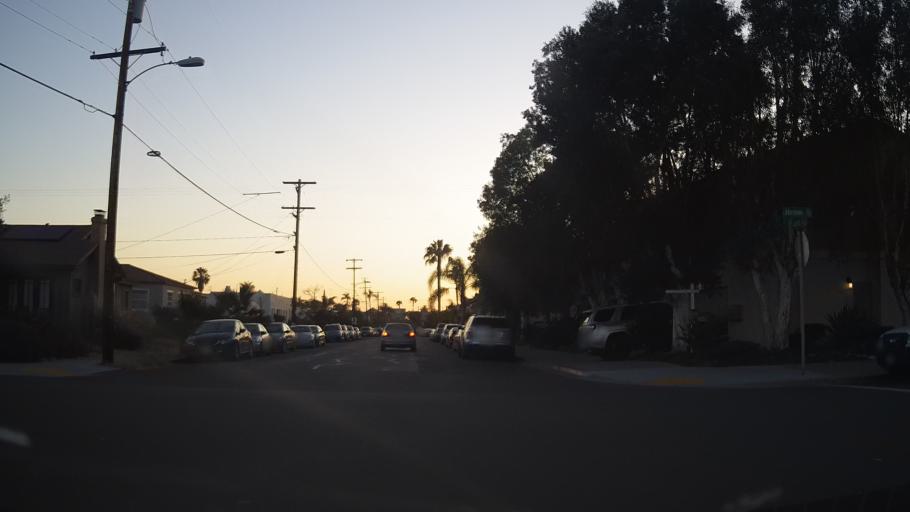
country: US
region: California
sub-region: San Diego County
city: San Diego
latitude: 32.7456
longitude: -117.1259
